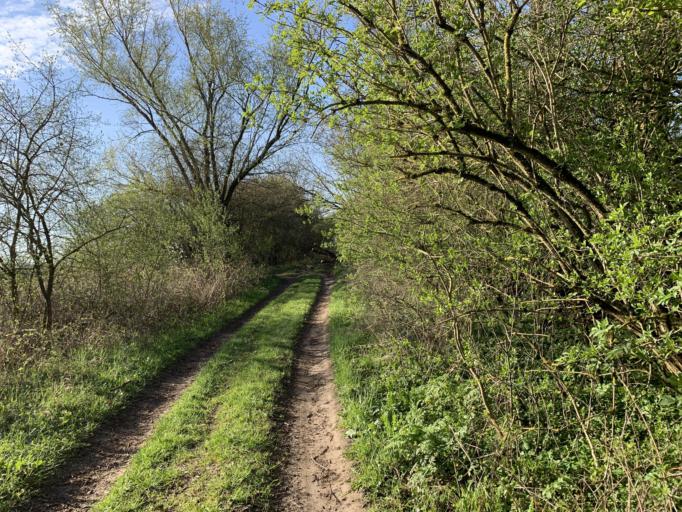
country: DE
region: Mecklenburg-Vorpommern
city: Blankensee
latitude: 53.4434
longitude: 13.2661
